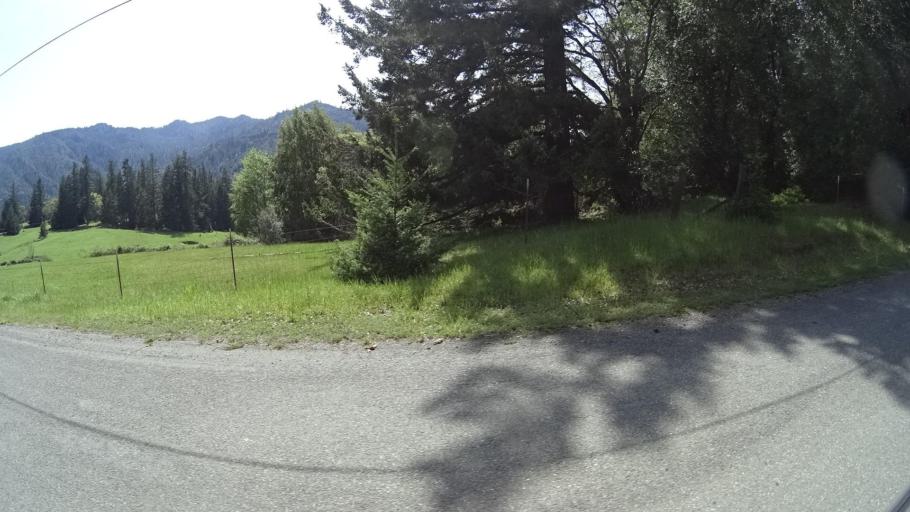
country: US
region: California
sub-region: Humboldt County
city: Redway
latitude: 40.3964
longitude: -123.7452
